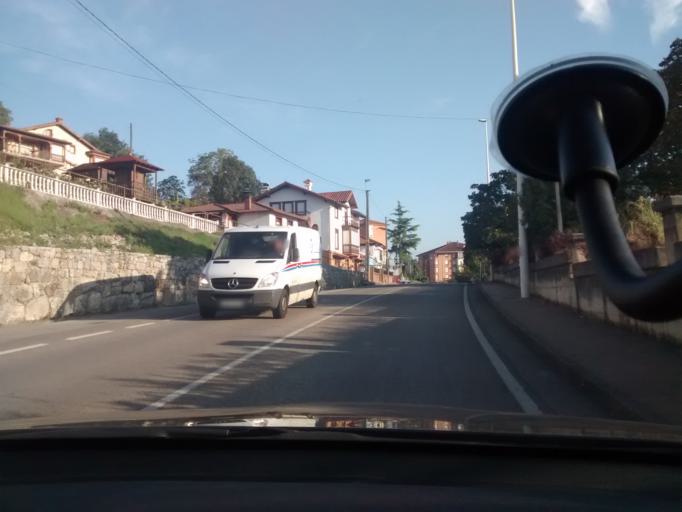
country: ES
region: Cantabria
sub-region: Provincia de Cantabria
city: Lierganes
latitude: 43.3810
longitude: -3.7322
